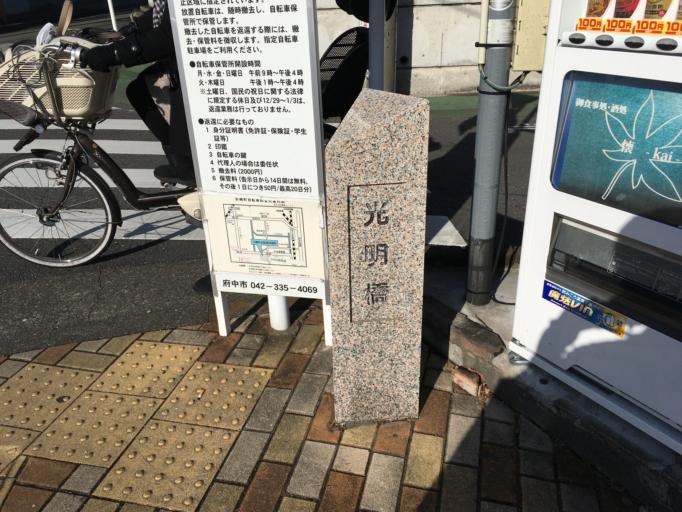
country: JP
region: Tokyo
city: Kokubunji
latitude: 35.6665
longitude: 139.4648
